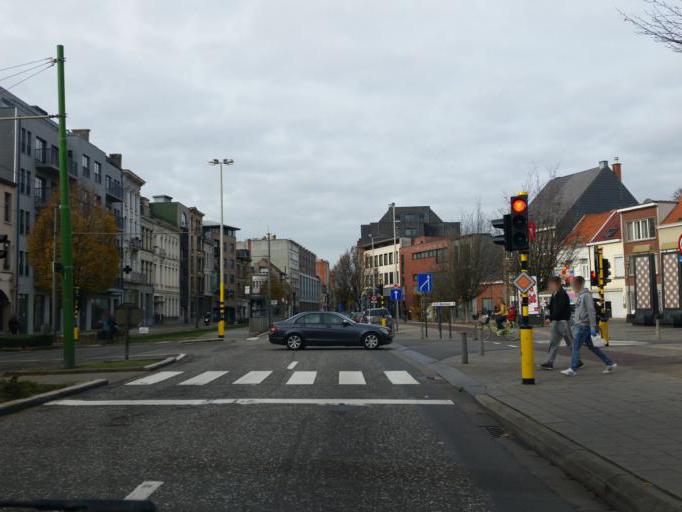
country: BE
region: Flanders
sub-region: Provincie Antwerpen
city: Antwerpen
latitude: 51.1953
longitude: 4.4192
